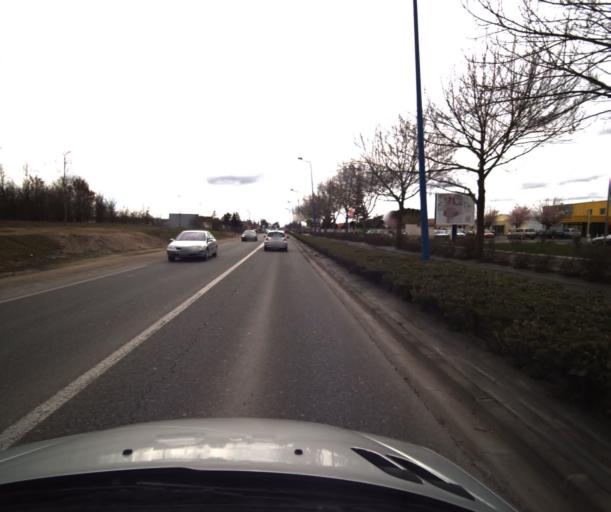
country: FR
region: Midi-Pyrenees
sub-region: Departement du Tarn-et-Garonne
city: Montauban
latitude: 44.0433
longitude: 1.3877
